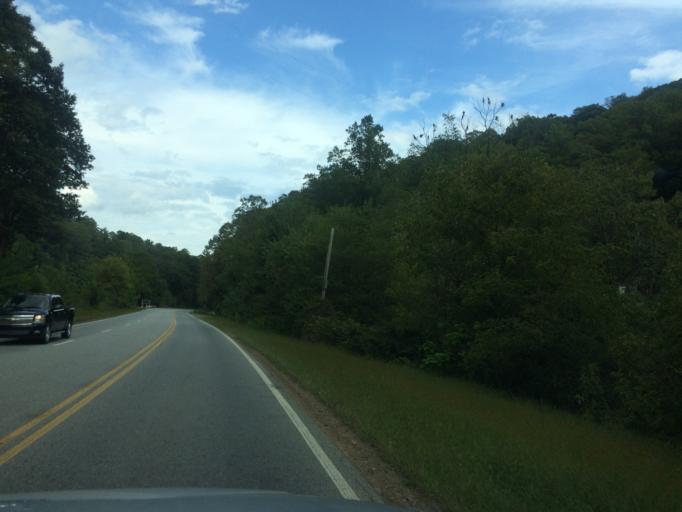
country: US
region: North Carolina
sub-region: Haywood County
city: Canton
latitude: 35.5378
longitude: -82.7789
